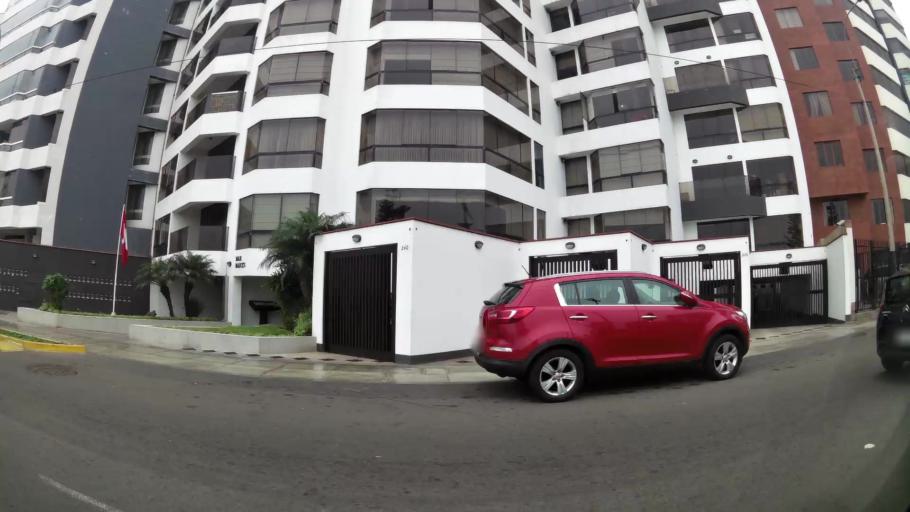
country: PE
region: Lima
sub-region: Lima
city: San Isidro
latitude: -12.1185
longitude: -77.0443
